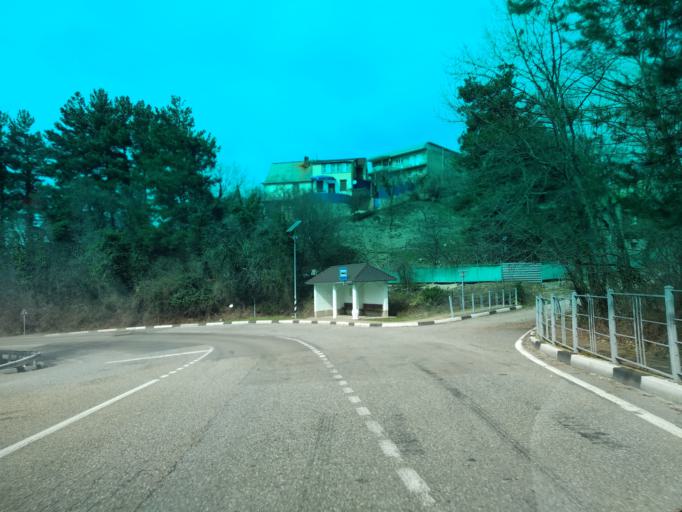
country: RU
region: Krasnodarskiy
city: Shepsi
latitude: 44.0452
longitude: 39.1354
